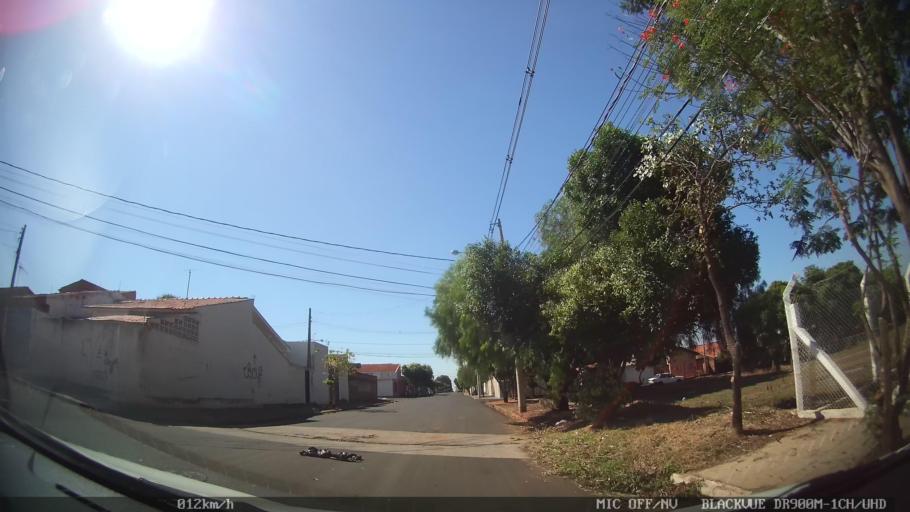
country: BR
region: Sao Paulo
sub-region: Sao Jose Do Rio Preto
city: Sao Jose do Rio Preto
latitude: -20.7719
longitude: -49.4127
